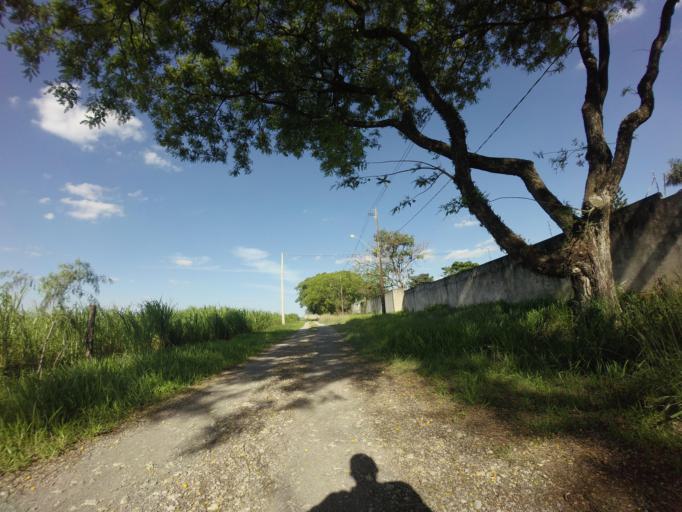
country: BR
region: Sao Paulo
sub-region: Piracicaba
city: Piracicaba
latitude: -22.7495
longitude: -47.5880
